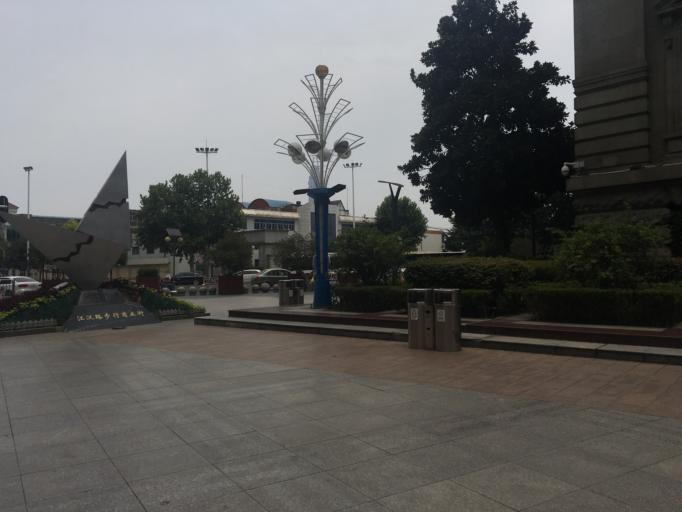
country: CN
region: Hubei
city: Wuhan
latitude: 30.5787
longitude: 114.2917
